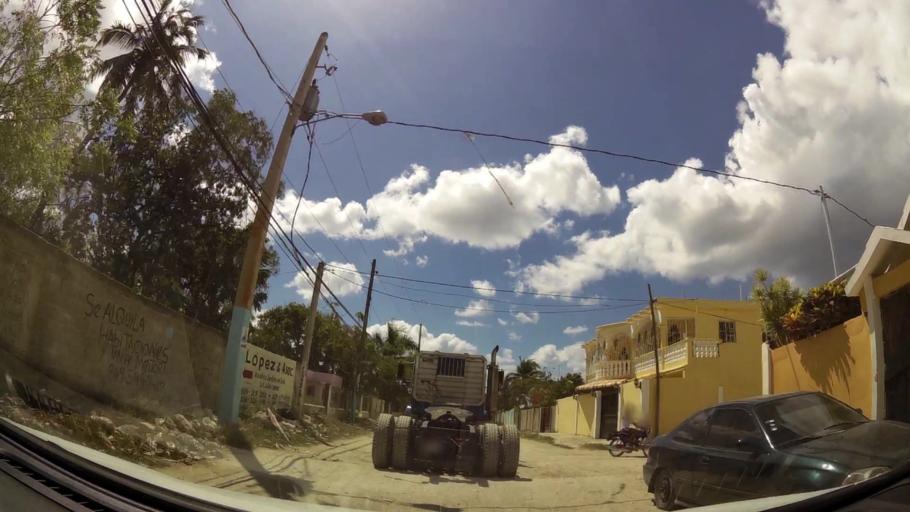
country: DO
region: Santo Domingo
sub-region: Santo Domingo
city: Boca Chica
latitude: 18.4508
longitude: -69.6497
